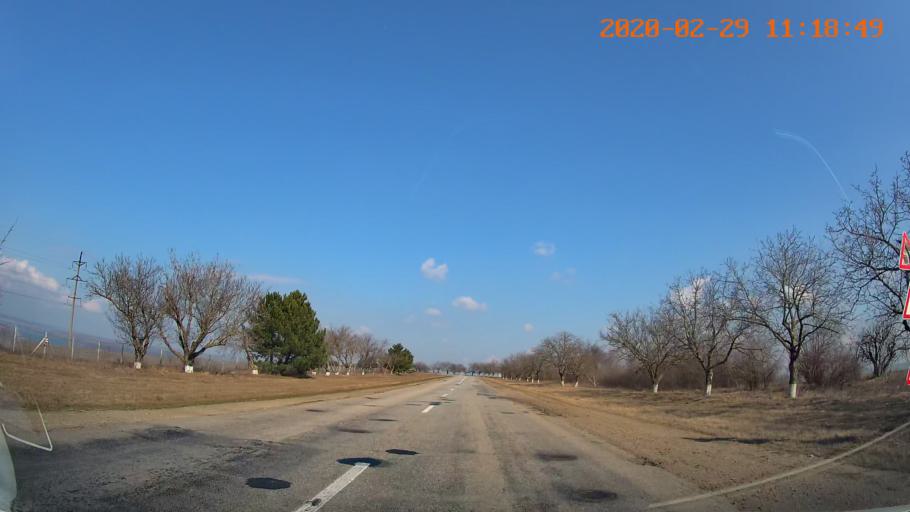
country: MD
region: Telenesti
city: Cocieri
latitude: 47.3404
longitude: 29.1753
